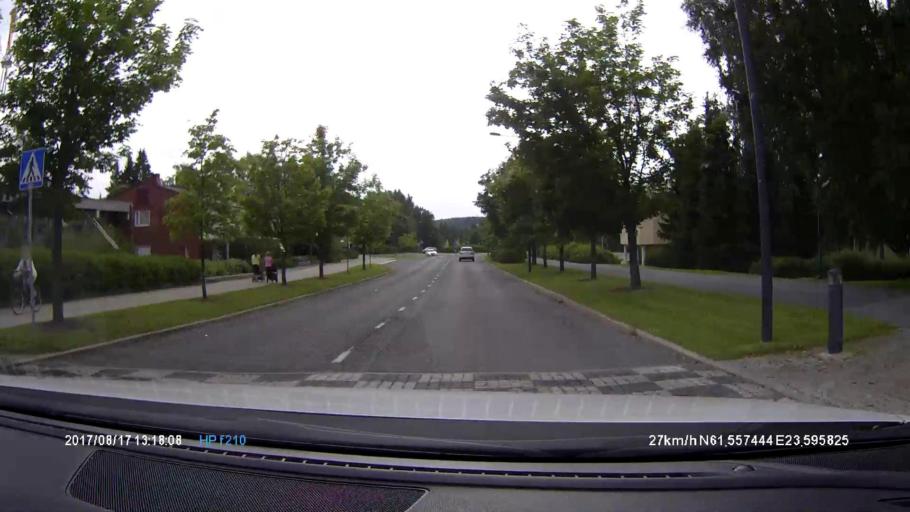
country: FI
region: Pirkanmaa
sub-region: Tampere
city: Yloejaervi
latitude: 61.5573
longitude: 23.5959
